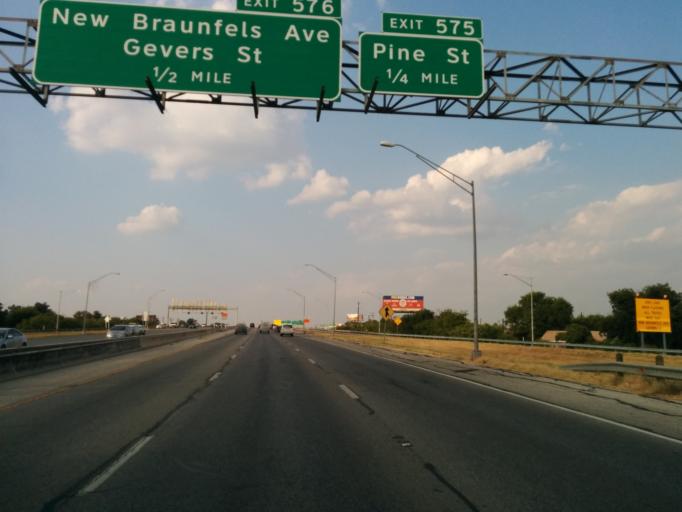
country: US
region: Texas
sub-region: Bexar County
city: San Antonio
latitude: 29.3966
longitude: -98.4760
